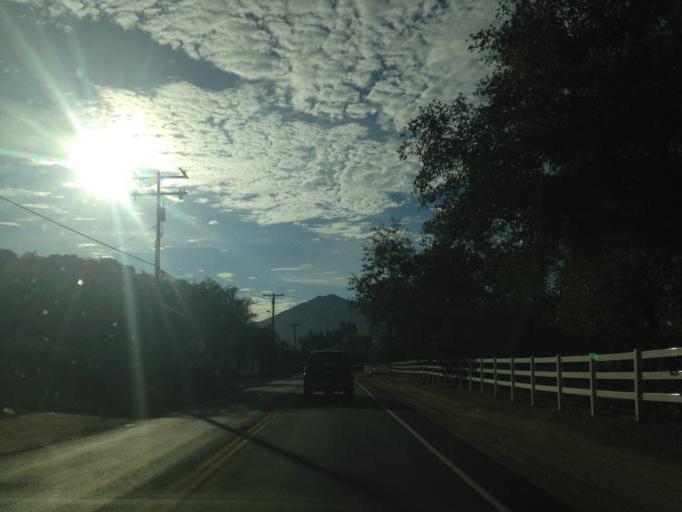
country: US
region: California
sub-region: San Diego County
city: Rainbow
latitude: 33.3779
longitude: -117.0820
